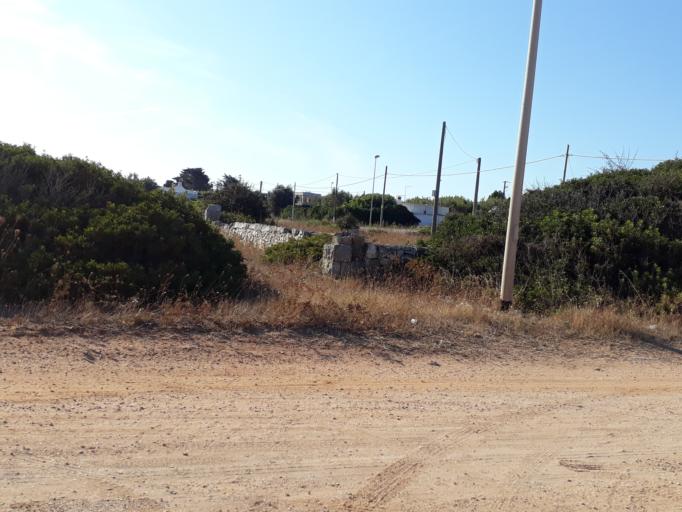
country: IT
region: Apulia
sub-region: Provincia di Brindisi
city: Carovigno
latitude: 40.7638
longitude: 17.6862
